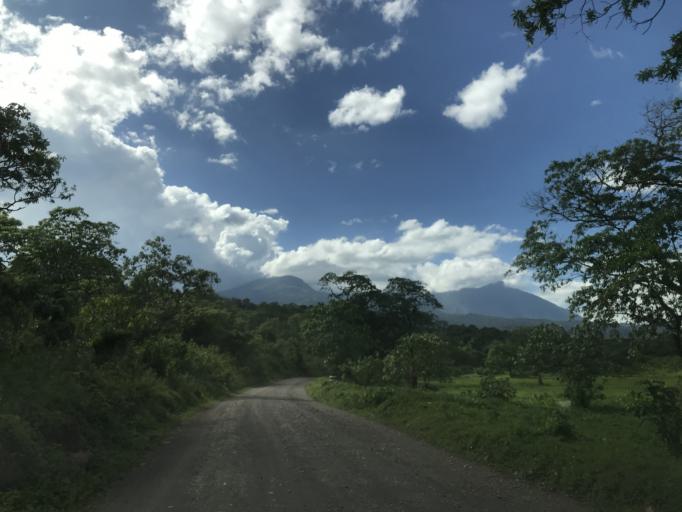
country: TZ
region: Arusha
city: Usa River
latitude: -3.3044
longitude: 36.8743
